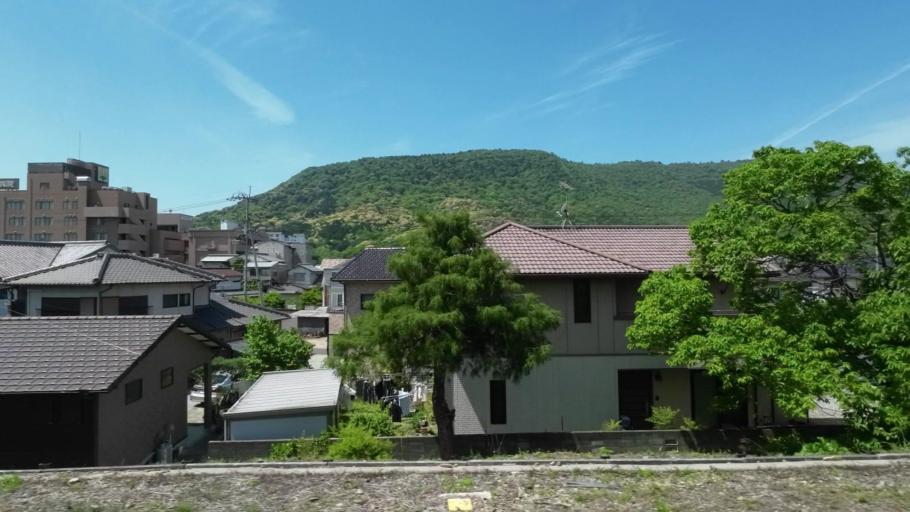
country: JP
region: Kagawa
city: Marugame
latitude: 34.1947
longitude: 133.8194
